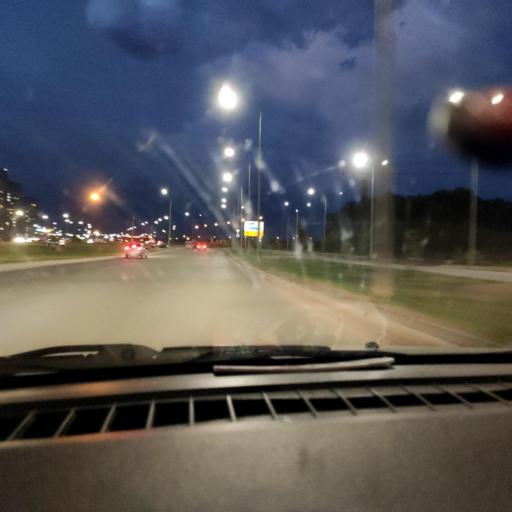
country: RU
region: Orenburg
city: Orenburg
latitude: 51.8063
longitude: 55.1697
